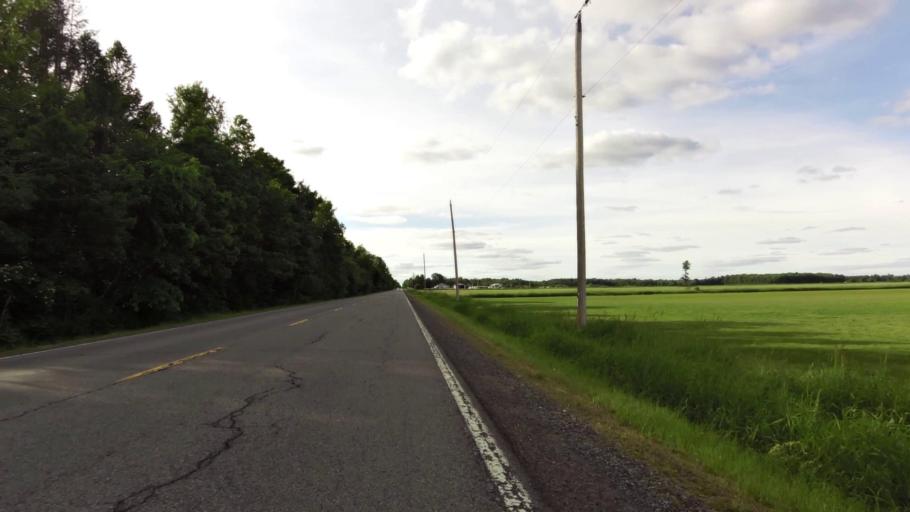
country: CA
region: Ontario
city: Ottawa
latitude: 45.1924
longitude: -75.5869
